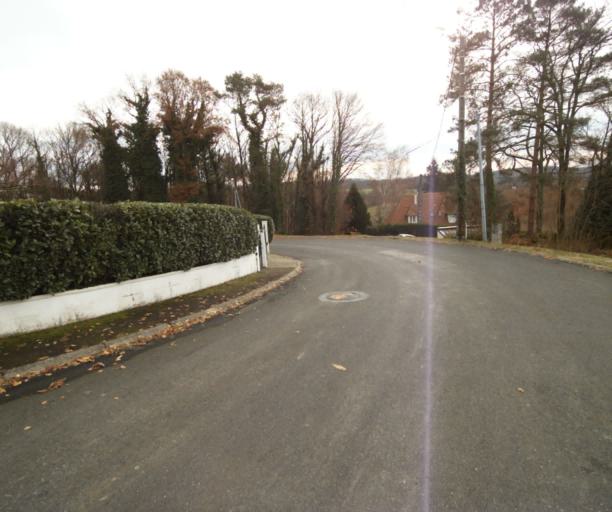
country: FR
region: Limousin
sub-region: Departement de la Correze
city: Saint-Mexant
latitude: 45.2678
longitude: 1.6811
